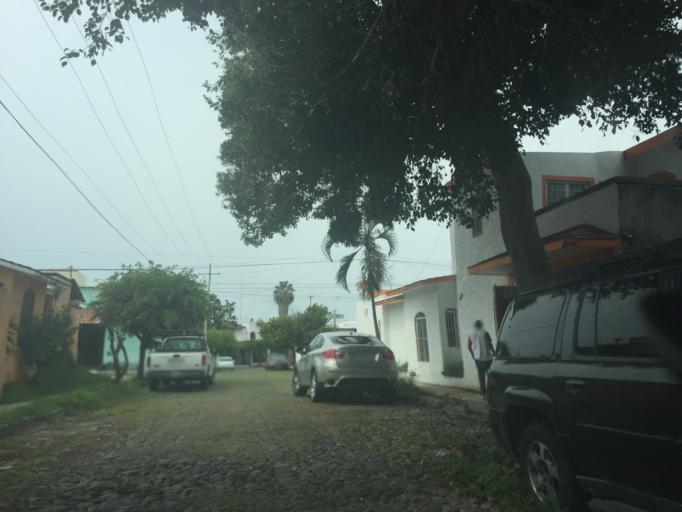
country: MX
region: Colima
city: Colima
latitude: 19.2633
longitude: -103.7156
